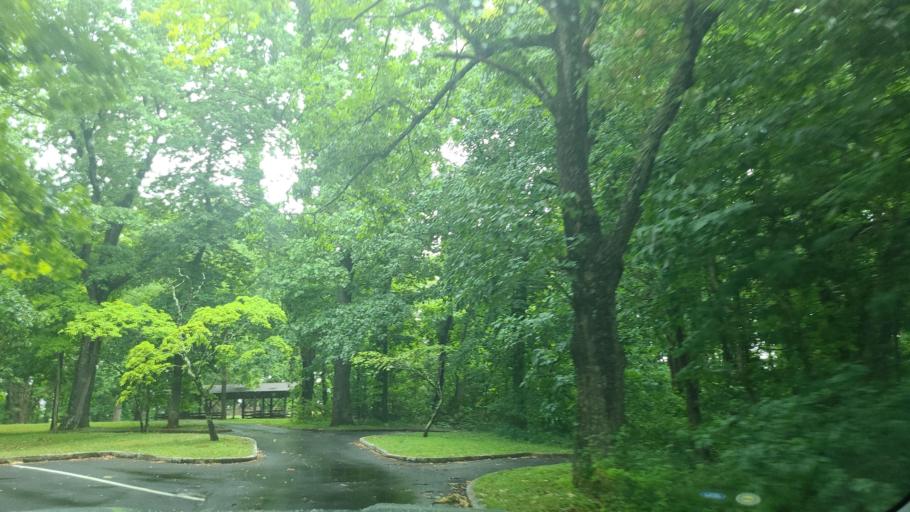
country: US
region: Virginia
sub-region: Floyd County
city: Floyd
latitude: 36.9290
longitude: -80.1854
